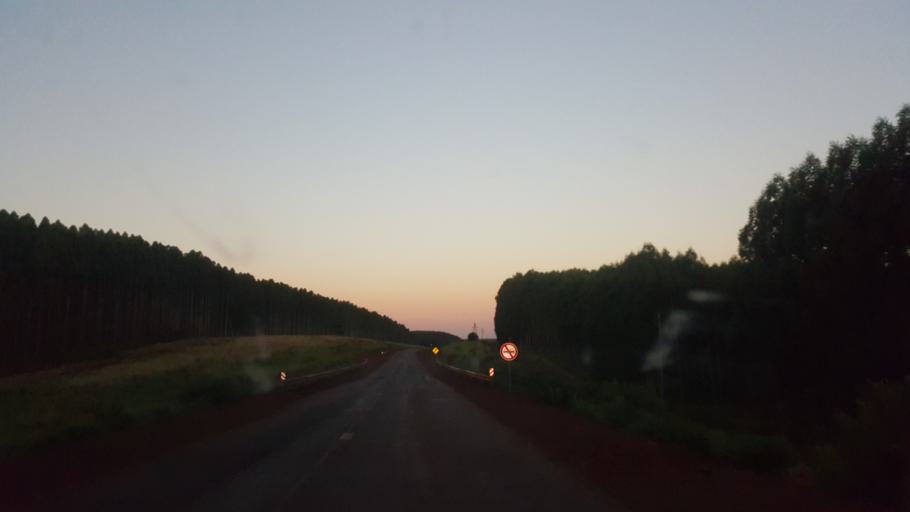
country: AR
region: Corrientes
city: Garruchos
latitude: -28.2492
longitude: -55.8446
